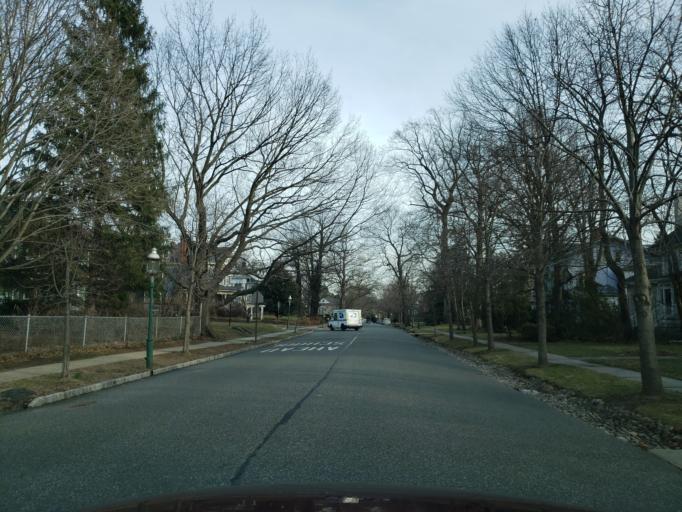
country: US
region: New Jersey
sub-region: Essex County
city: Glen Ridge
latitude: 40.7926
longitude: -74.2098
